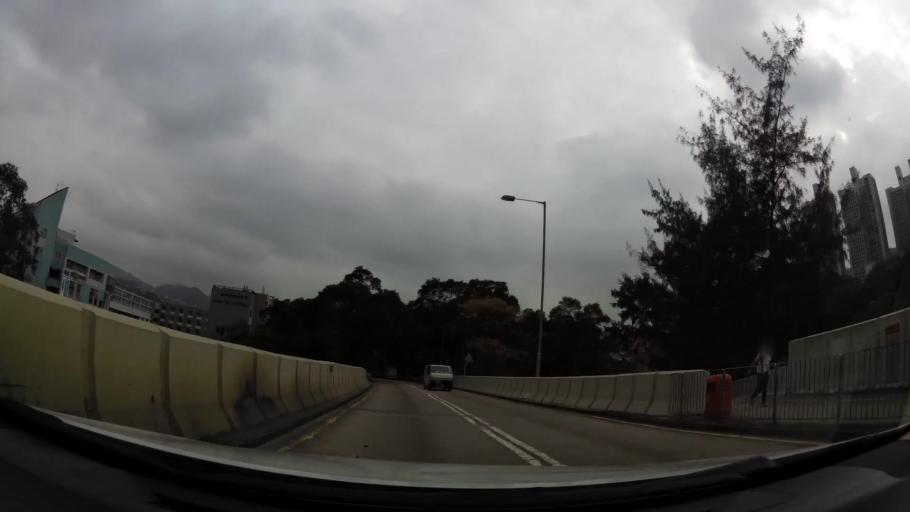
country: HK
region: Sha Tin
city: Sha Tin
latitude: 22.3938
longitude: 114.1978
